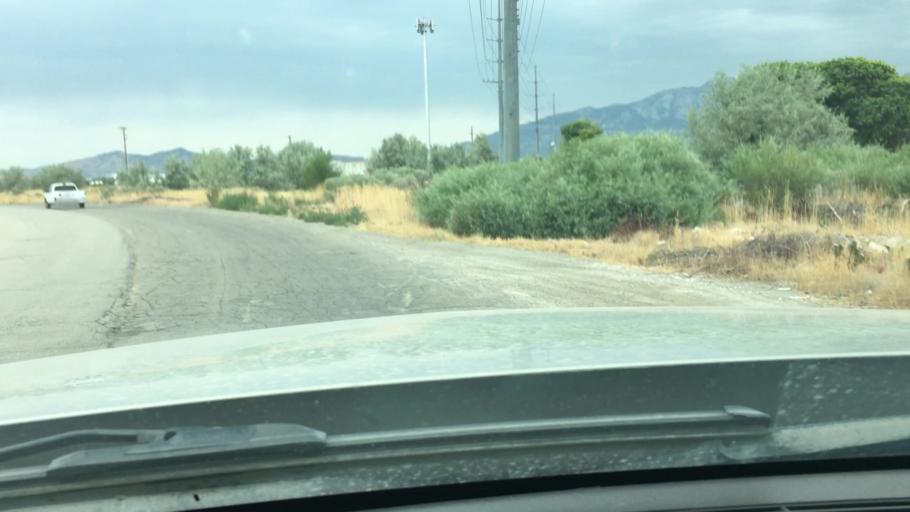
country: US
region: Utah
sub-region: Utah County
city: American Fork
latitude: 40.3532
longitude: -111.7857
